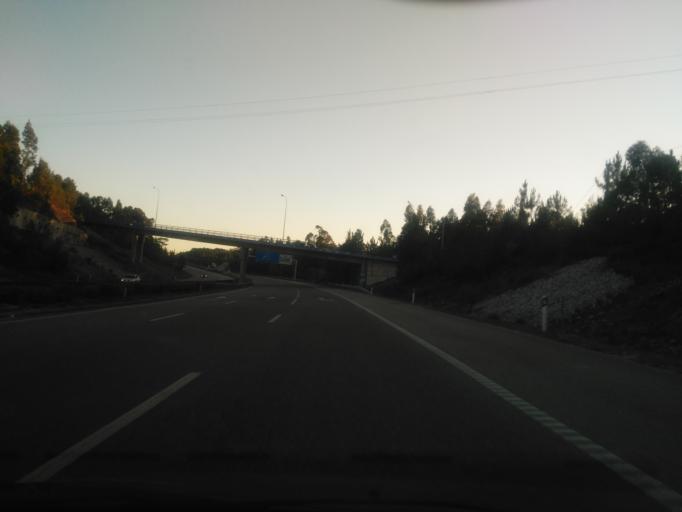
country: PT
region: Leiria
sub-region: Leiria
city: Maceira
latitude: 39.7193
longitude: -8.9113
